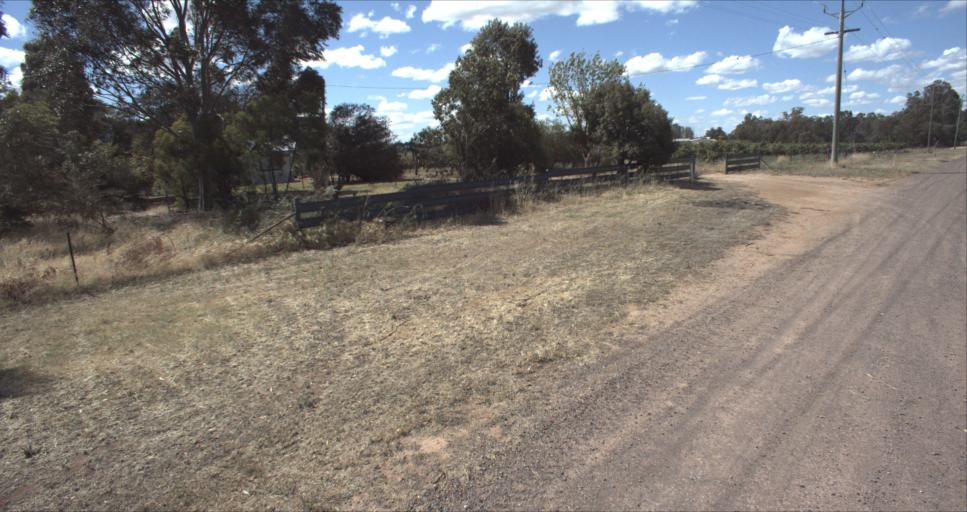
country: AU
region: New South Wales
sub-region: Leeton
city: Leeton
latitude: -34.5167
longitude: 146.2298
